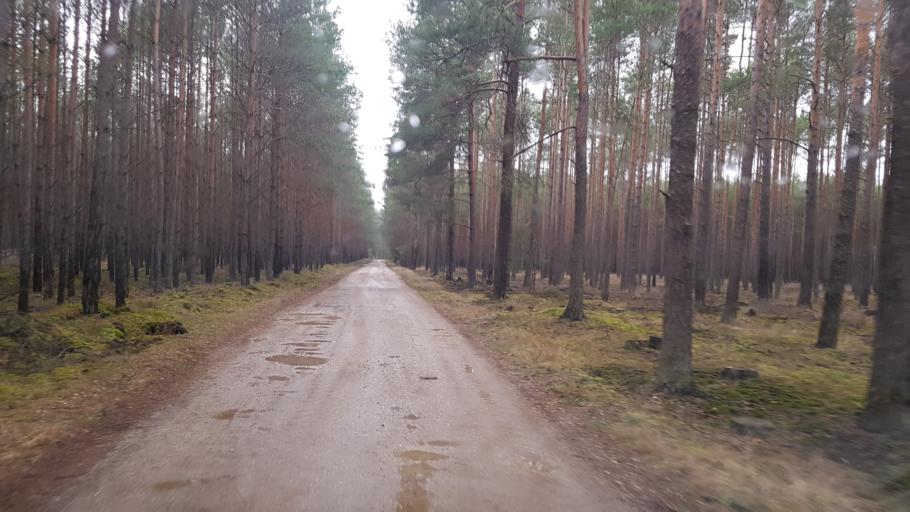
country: DE
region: Brandenburg
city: Sallgast
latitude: 51.6615
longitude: 13.8301
